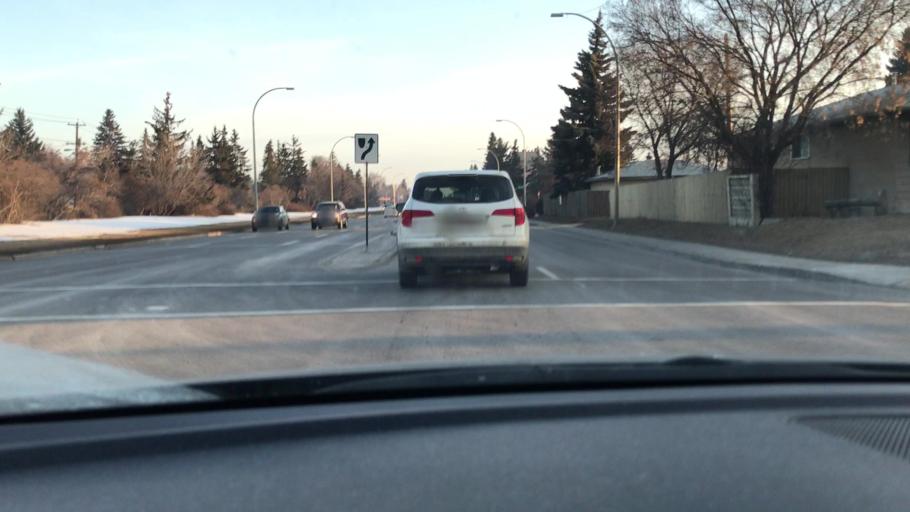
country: CA
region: Alberta
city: Edmonton
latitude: 53.5212
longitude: -113.4429
